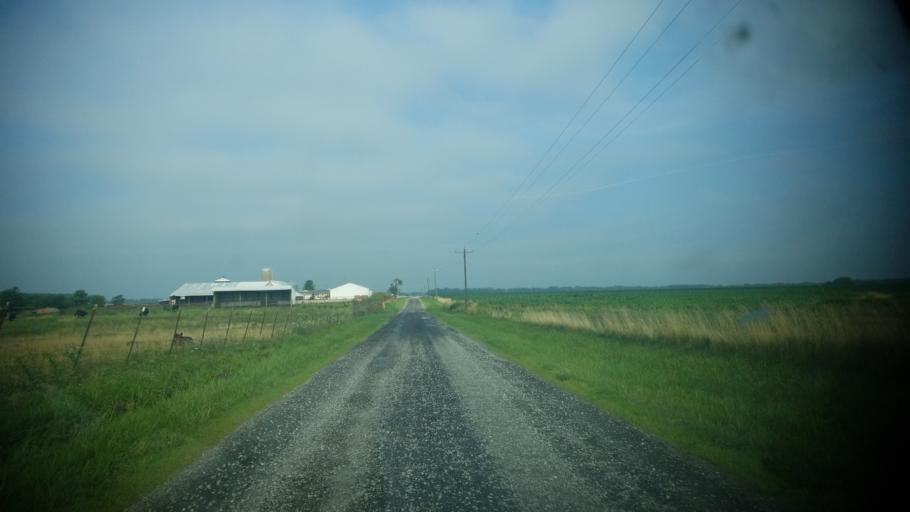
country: US
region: Illinois
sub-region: Clay County
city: Flora
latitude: 38.6014
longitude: -88.3374
